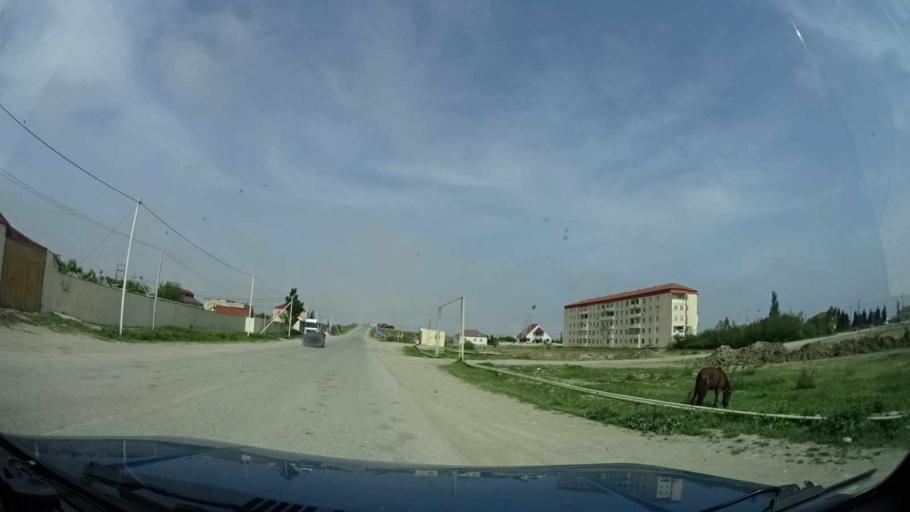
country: AZ
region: Xizi
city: Kilyazi
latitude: 40.8677
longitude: 49.3502
